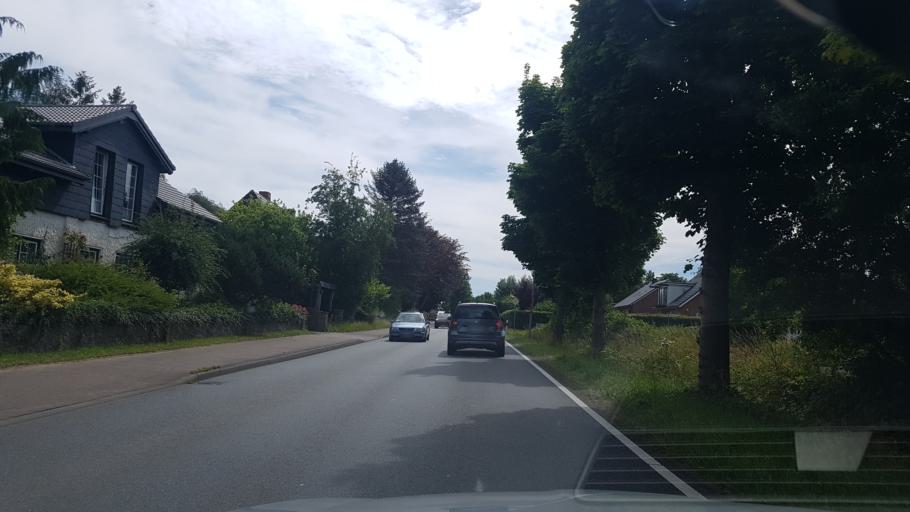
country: DE
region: Schleswig-Holstein
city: Gross Buchwald
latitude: 54.1631
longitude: 10.0800
